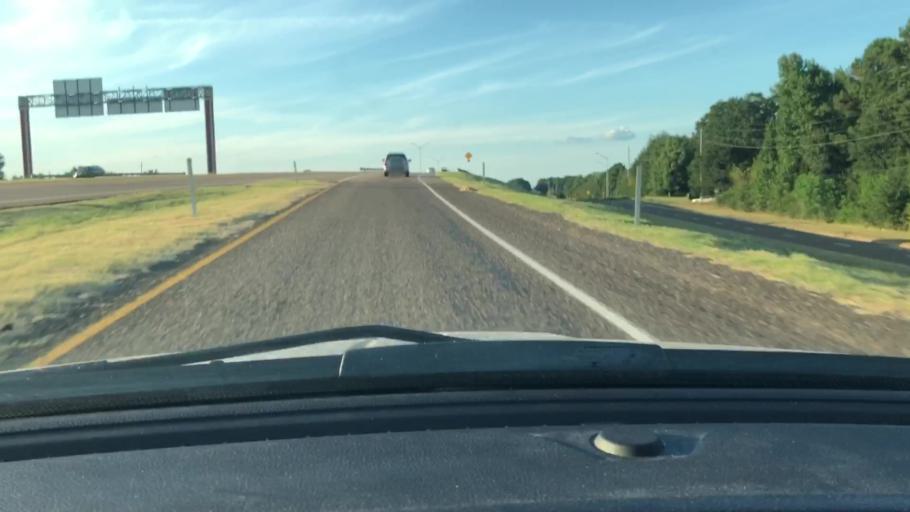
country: US
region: Texas
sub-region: Bowie County
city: Wake Village
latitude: 33.4000
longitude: -94.0973
